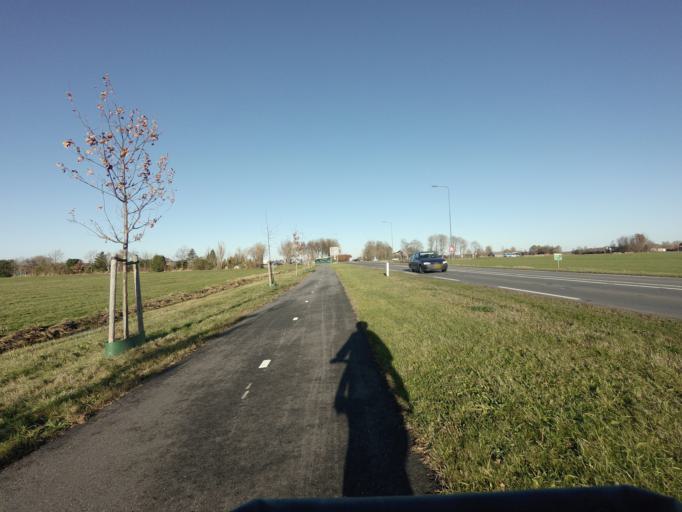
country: NL
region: Utrecht
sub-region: Gemeente De Ronde Venen
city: Mijdrecht
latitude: 52.2051
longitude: 4.9044
